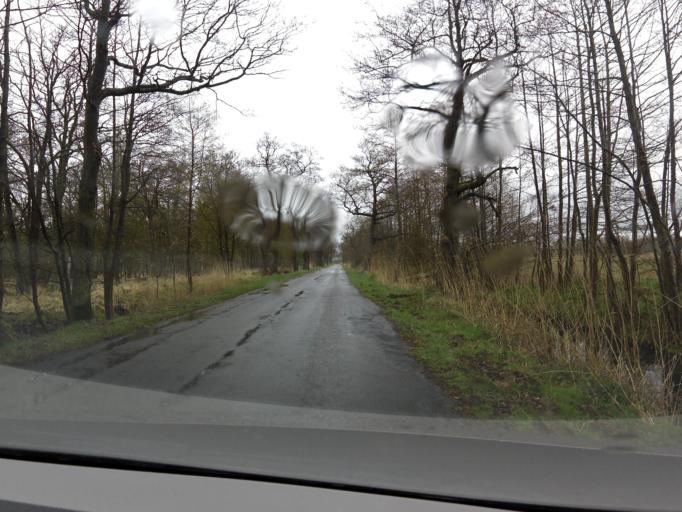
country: DE
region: Mecklenburg-Vorpommern
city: Barth
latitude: 54.4218
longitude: 12.7898
